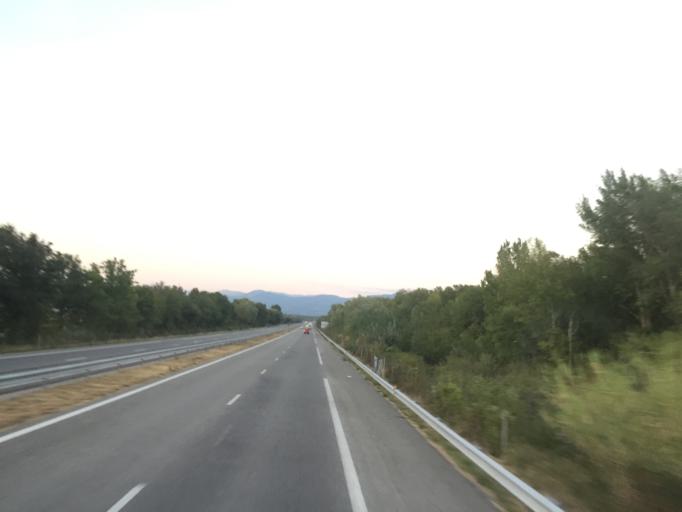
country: FR
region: Provence-Alpes-Cote d'Azur
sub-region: Departement des Alpes-de-Haute-Provence
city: Peyruis
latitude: 44.0199
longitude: 5.9454
